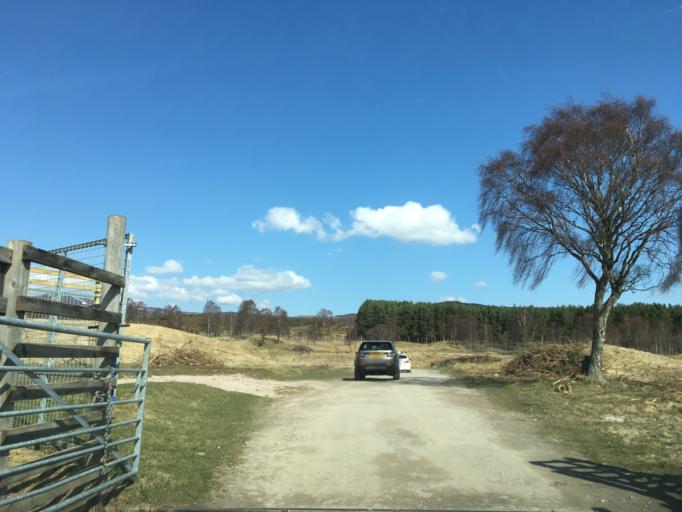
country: GB
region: Scotland
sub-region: Highland
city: Kingussie
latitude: 57.1125
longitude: -3.9816
